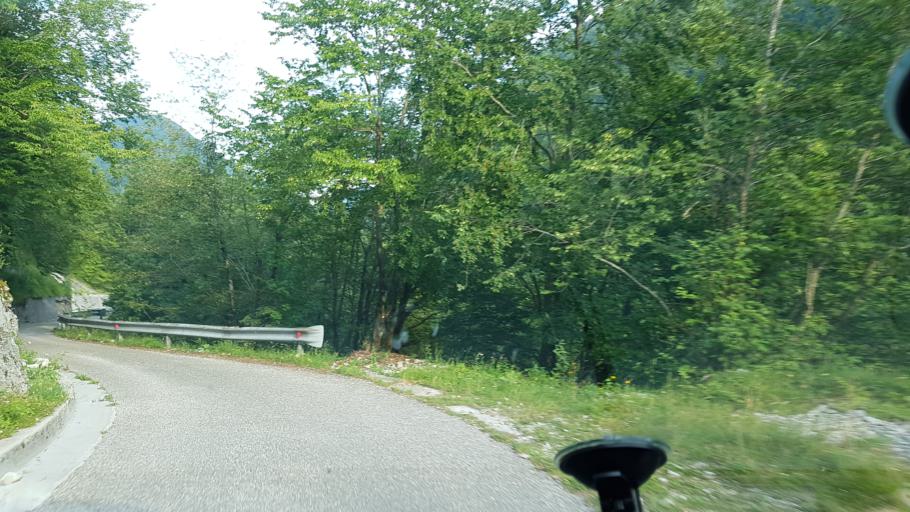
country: IT
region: Friuli Venezia Giulia
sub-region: Provincia di Udine
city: Taipana
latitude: 46.3253
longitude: 13.3736
